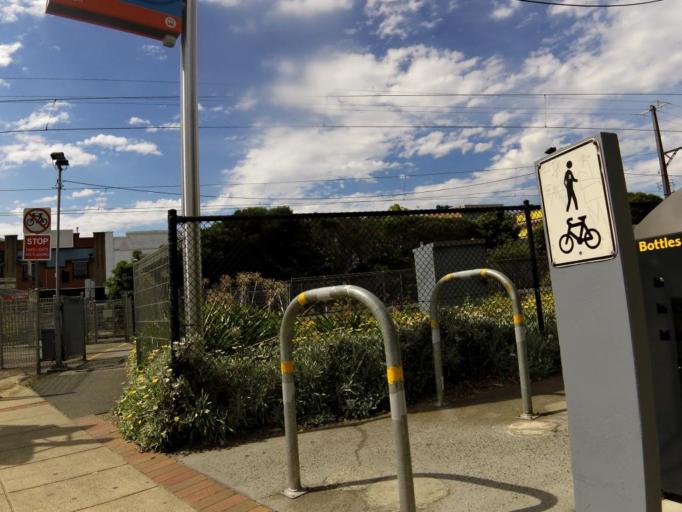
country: AU
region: Victoria
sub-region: Glen Eira
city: Murrumbeena
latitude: -37.8947
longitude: 145.0768
